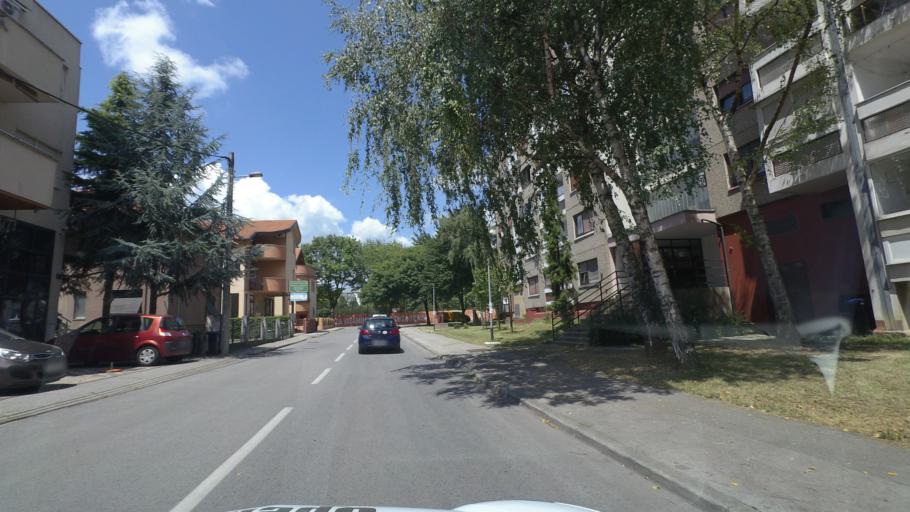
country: HR
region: Grad Zagreb
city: Dubrava
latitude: 45.8166
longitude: 16.0257
